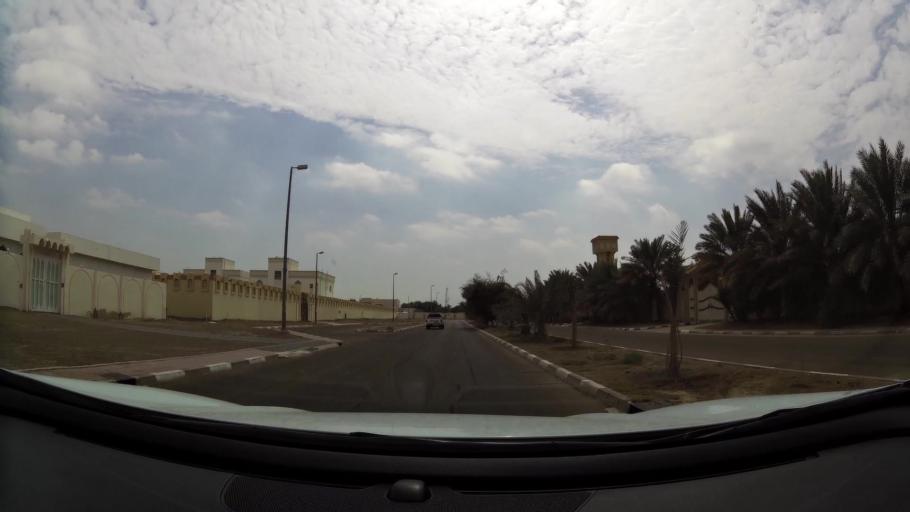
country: AE
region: Abu Dhabi
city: Al Ain
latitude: 24.2017
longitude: 55.7912
